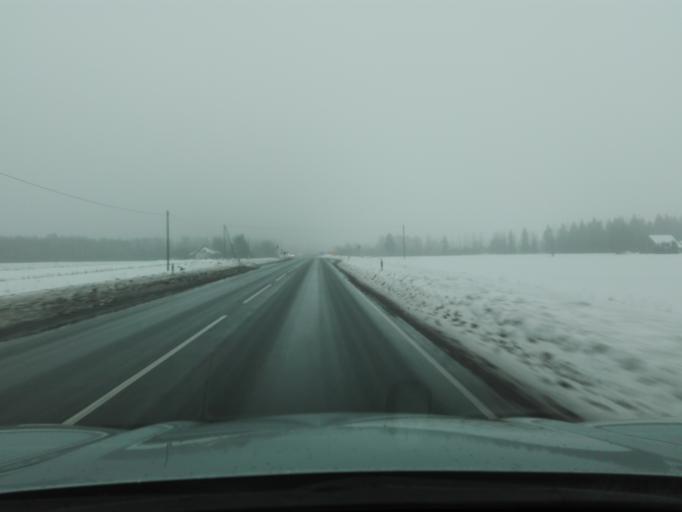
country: EE
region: Raplamaa
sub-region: Kohila vald
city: Kohila
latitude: 59.2014
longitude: 24.7828
